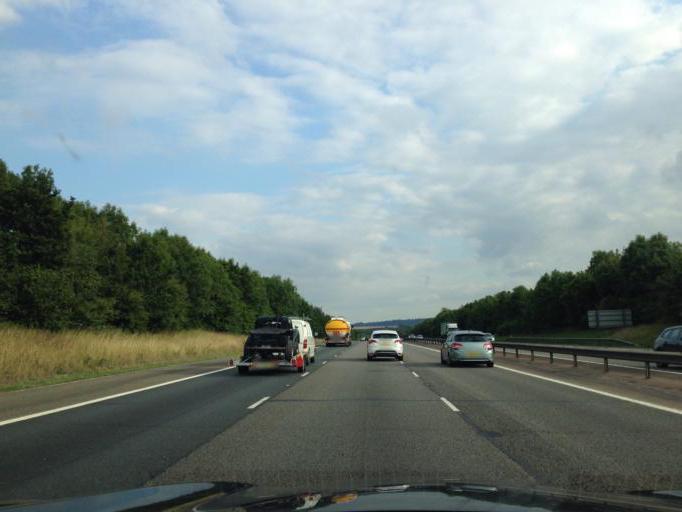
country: GB
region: England
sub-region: Warwickshire
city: Harbury
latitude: 52.1818
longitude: -1.4475
